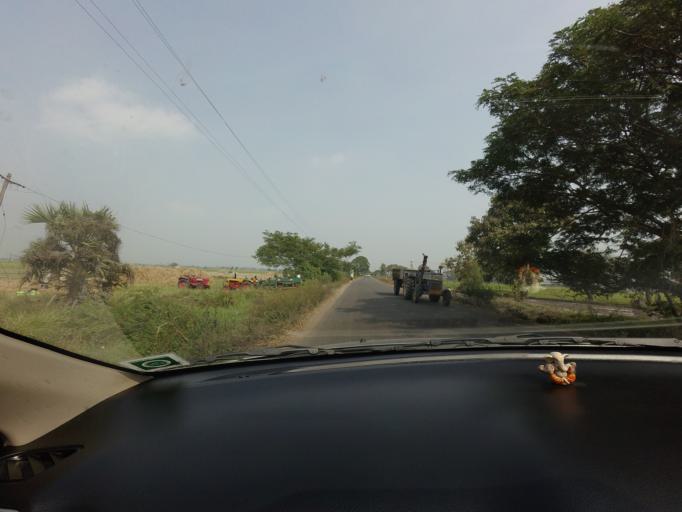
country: IN
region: Andhra Pradesh
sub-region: Krishna
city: Kankipadu
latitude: 16.4540
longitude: 80.7764
